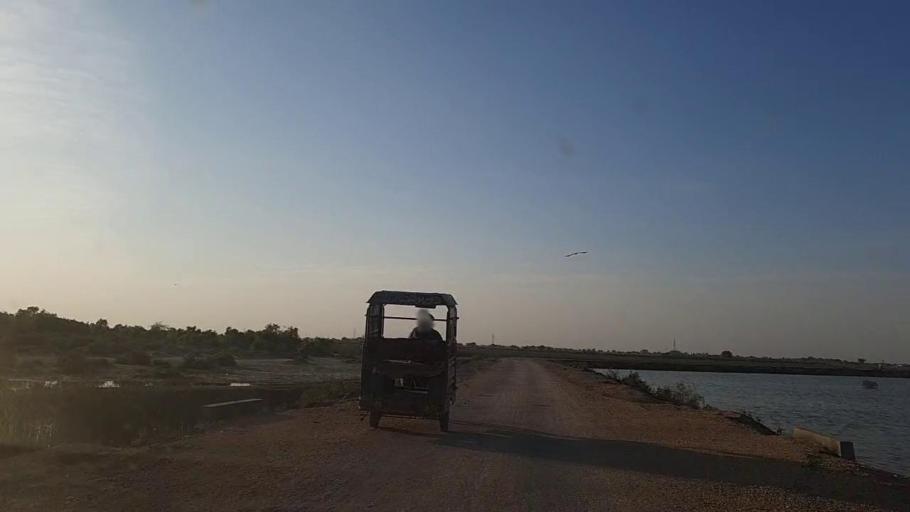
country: PK
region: Sindh
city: Mirpur Batoro
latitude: 24.6866
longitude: 68.2045
